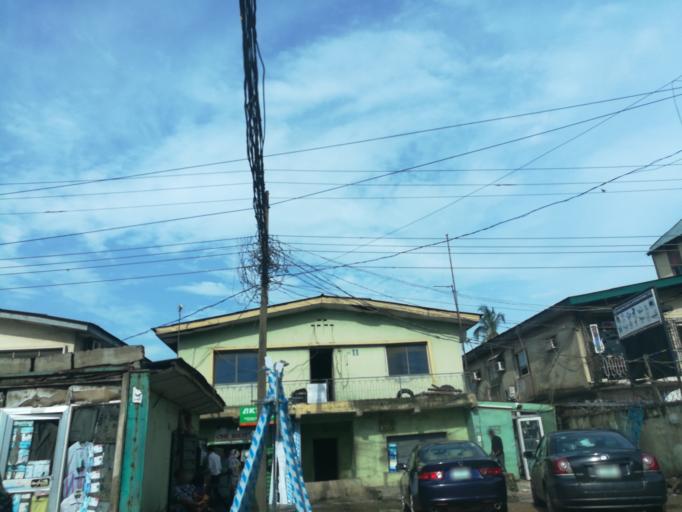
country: NG
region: Lagos
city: Ikeja
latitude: 6.5988
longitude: 3.3434
